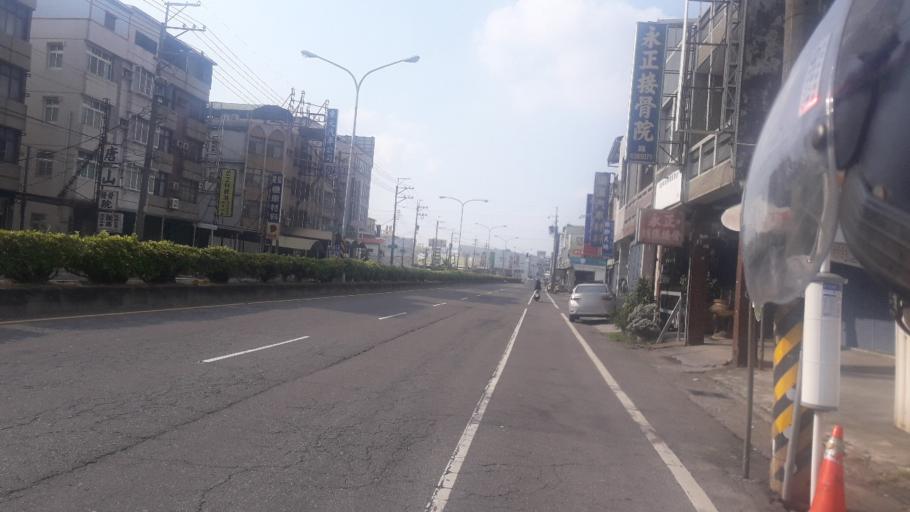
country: TW
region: Taiwan
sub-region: Tainan
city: Tainan
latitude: 22.8629
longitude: 120.2580
